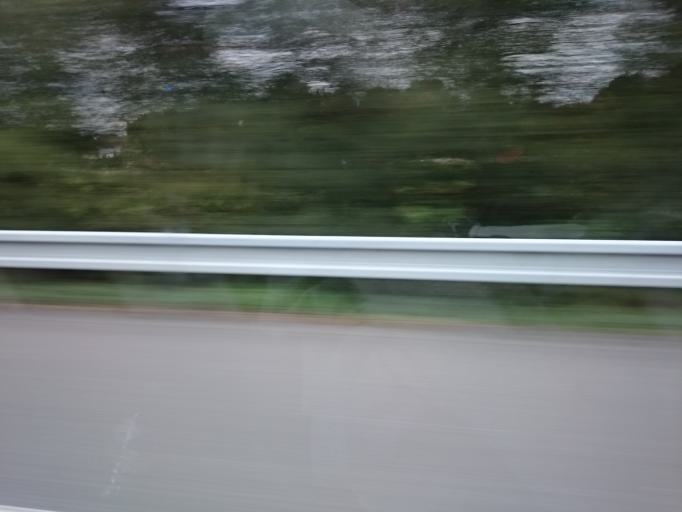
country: FR
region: Brittany
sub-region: Departement du Morbihan
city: Landevant
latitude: 47.7567
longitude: -3.1256
